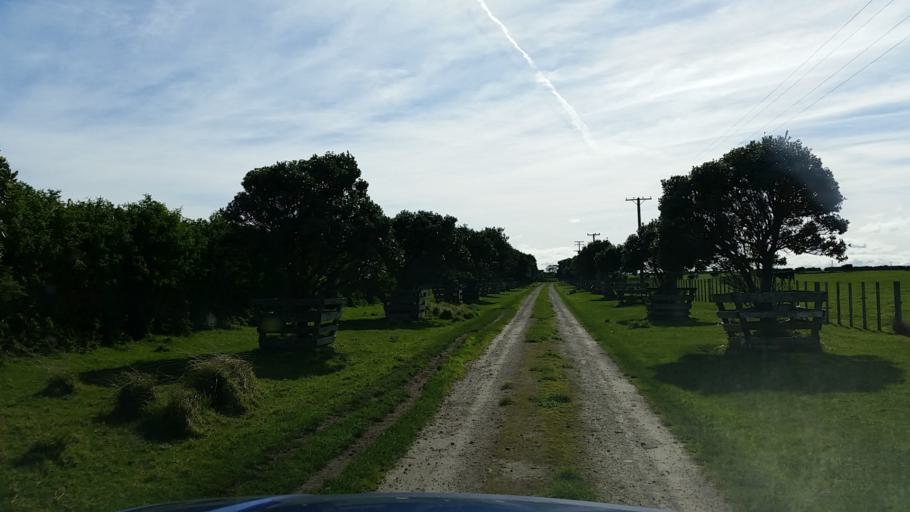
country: NZ
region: Taranaki
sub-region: South Taranaki District
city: Patea
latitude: -39.7688
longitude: 174.4935
